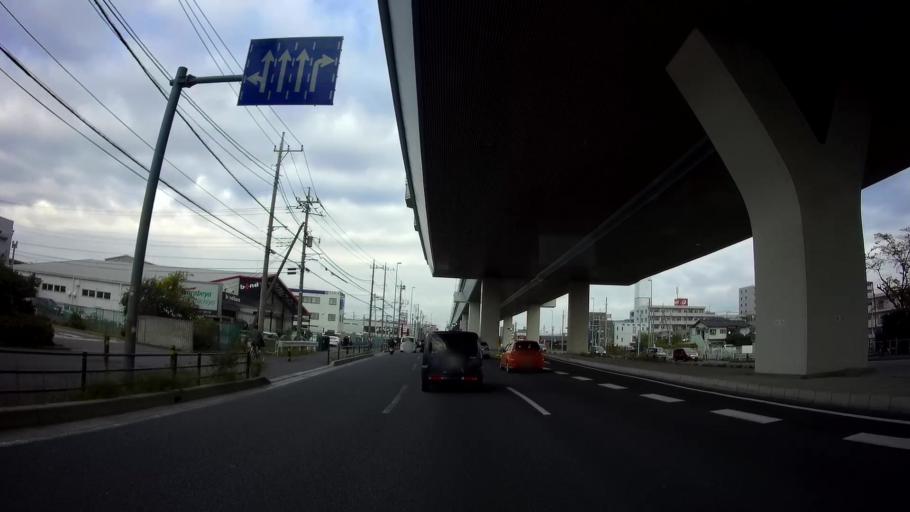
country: JP
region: Saitama
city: Yono
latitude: 35.8542
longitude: 139.6234
